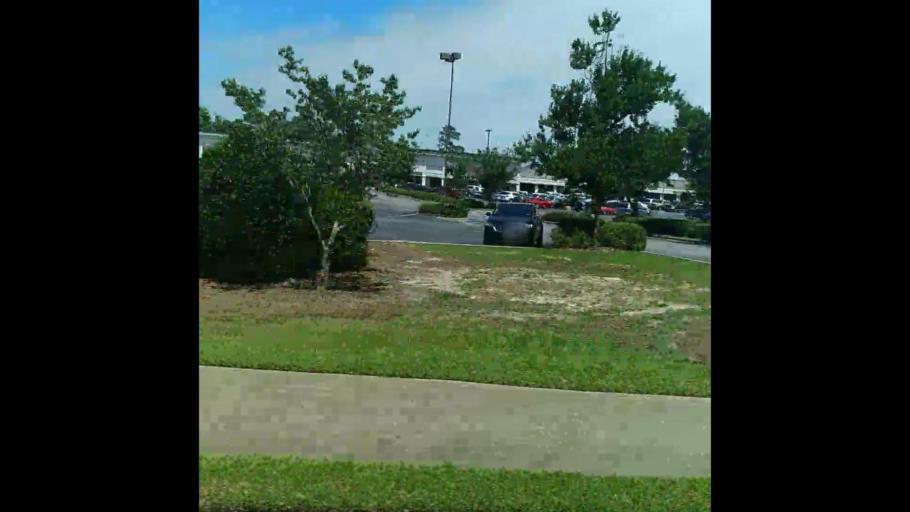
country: US
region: South Carolina
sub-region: Lexington County
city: West Columbia
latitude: 33.9873
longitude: -81.0565
